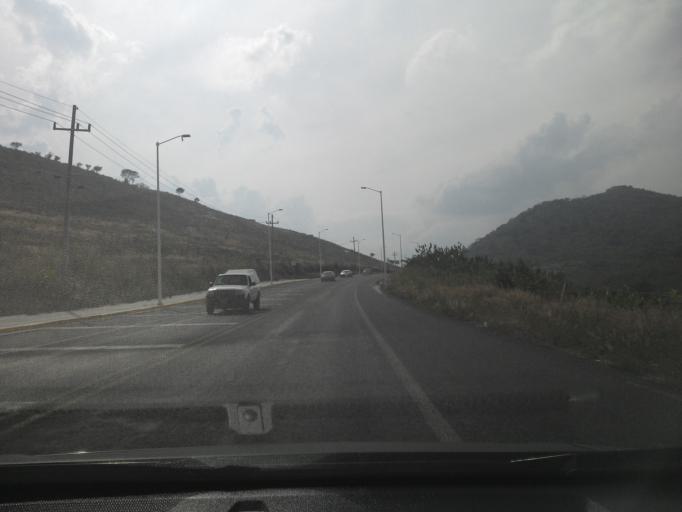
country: MX
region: Jalisco
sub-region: Tlajomulco de Zuniga
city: Lomas del Sur
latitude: 20.4889
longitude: -103.4208
